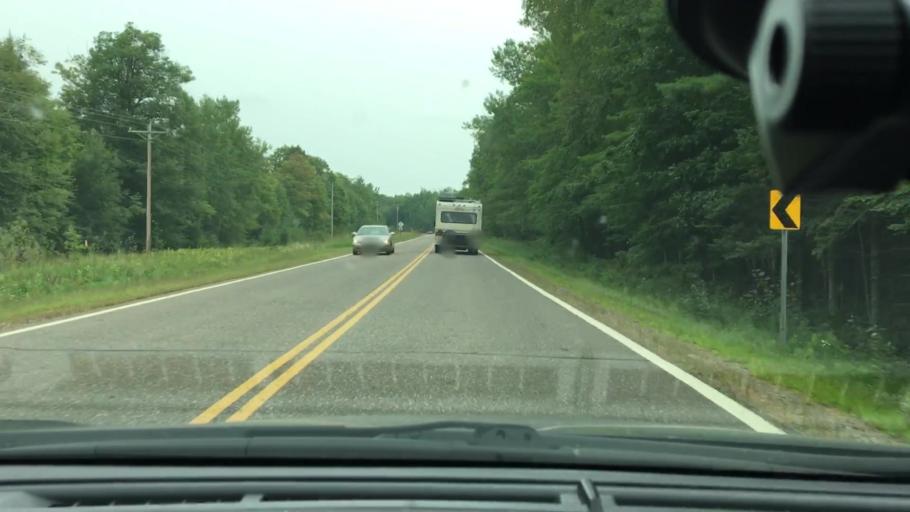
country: US
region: Minnesota
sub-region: Aitkin County
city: Aitkin
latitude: 46.4020
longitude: -93.7988
